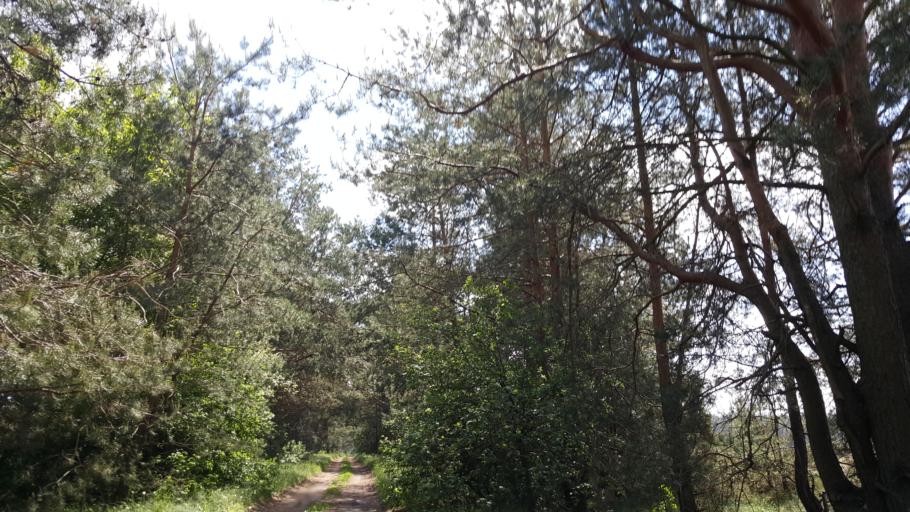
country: BY
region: Brest
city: Kamyanyets
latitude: 52.3964
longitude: 23.8602
